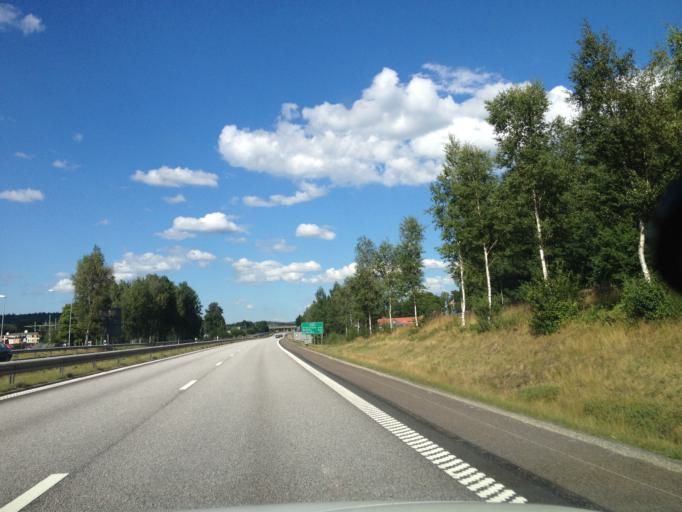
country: SE
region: Vaestra Goetaland
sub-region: Lerums Kommun
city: Lerum
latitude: 57.7614
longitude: 12.2584
